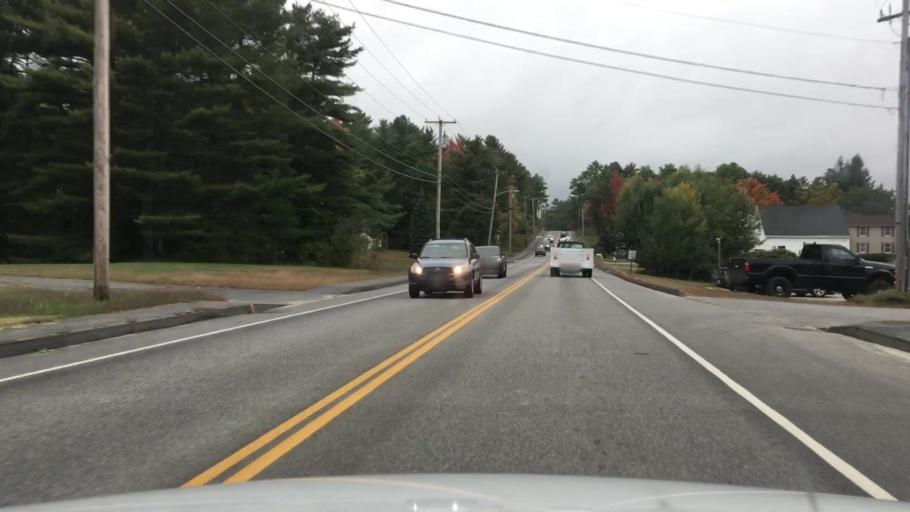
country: US
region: Maine
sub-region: Androscoggin County
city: Poland
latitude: 44.0640
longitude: -70.3976
